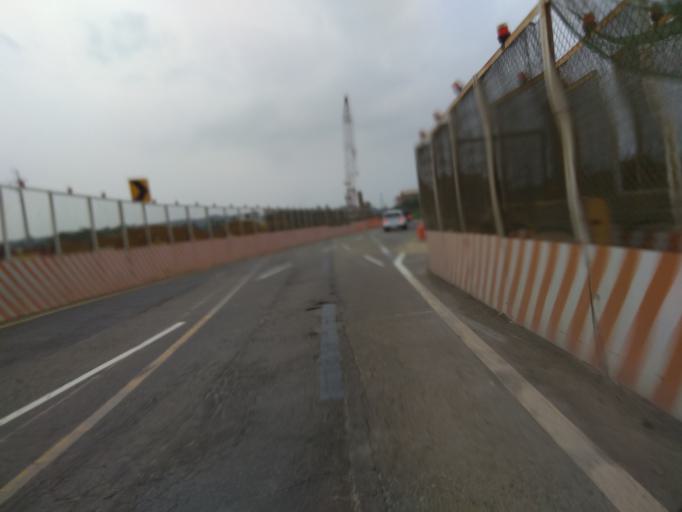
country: TW
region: Taiwan
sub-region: Hsinchu
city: Zhubei
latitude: 24.9003
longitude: 120.9704
